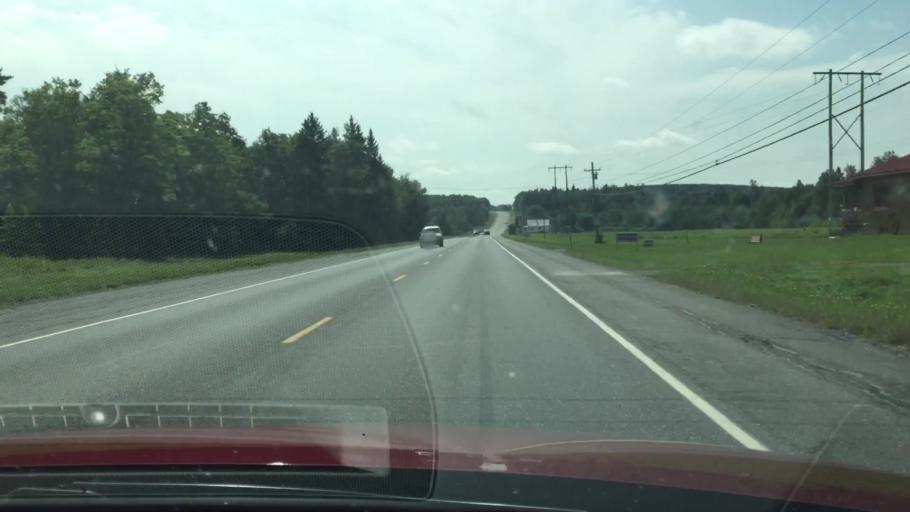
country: US
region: Maine
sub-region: Aroostook County
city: Easton
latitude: 46.4787
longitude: -67.8684
